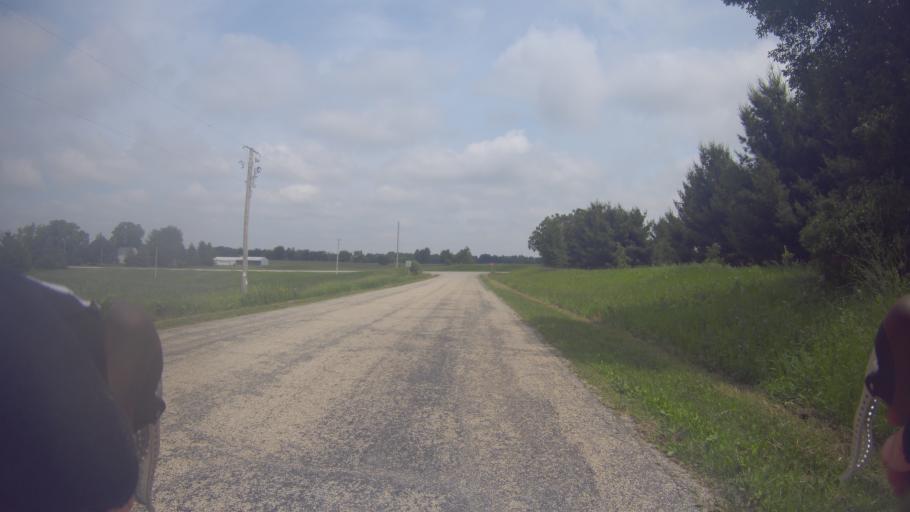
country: US
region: Wisconsin
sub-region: Jefferson County
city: Lake Ripley
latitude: 42.9487
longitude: -88.9889
